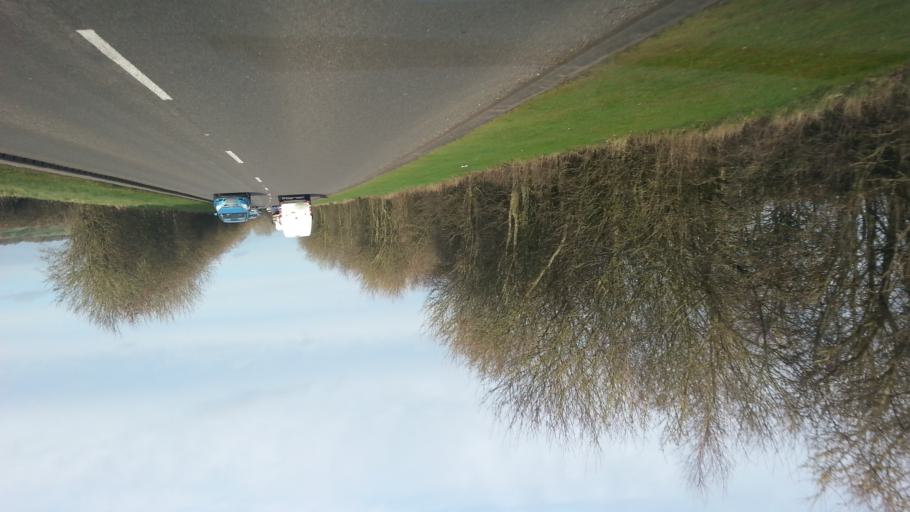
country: GB
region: England
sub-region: Staffordshire
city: Colwich
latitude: 52.8643
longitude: -1.9505
